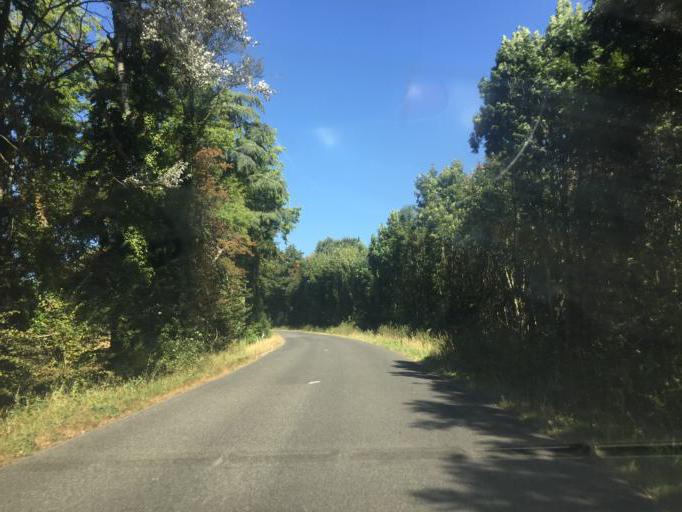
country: FR
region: Rhone-Alpes
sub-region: Departement de l'Ain
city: Tramoyes
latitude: 45.8935
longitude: 4.9706
